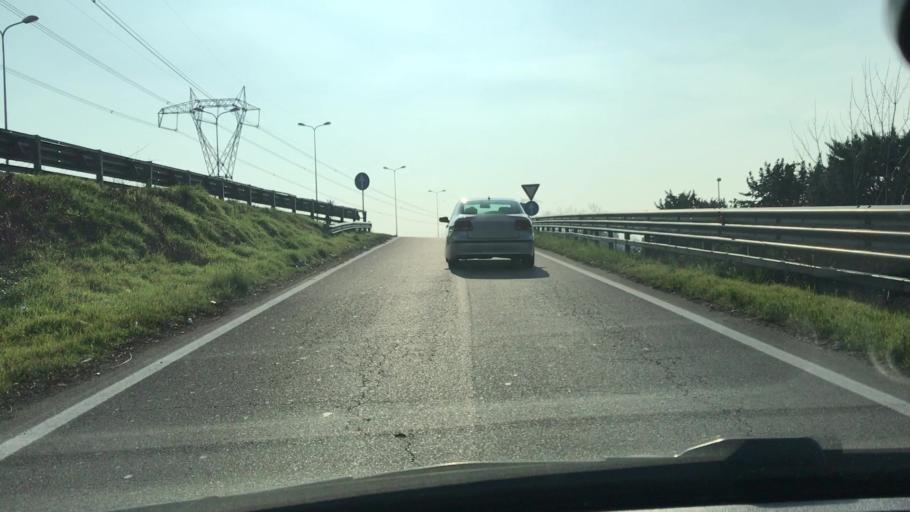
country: IT
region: Lombardy
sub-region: Provincia di Monza e Brianza
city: Cesano Maderno
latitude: 45.6302
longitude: 9.1622
